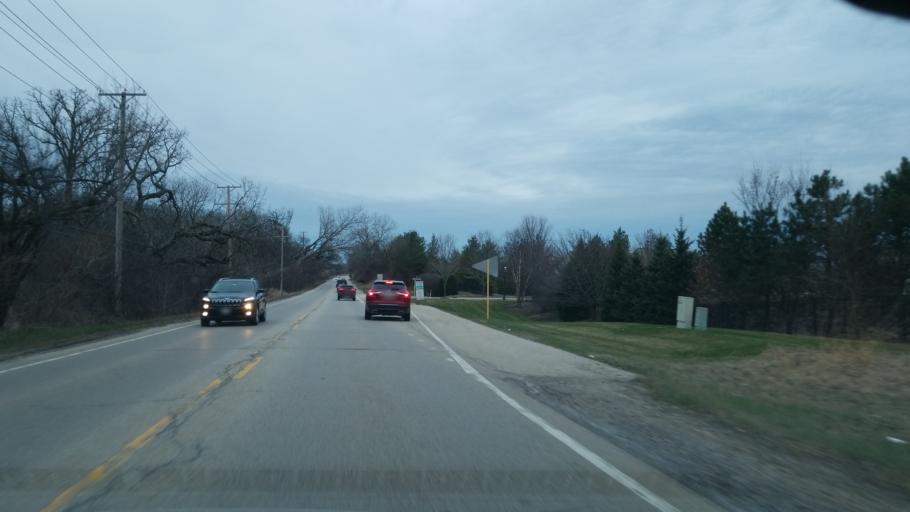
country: US
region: Illinois
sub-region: Kane County
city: Sleepy Hollow
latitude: 42.1032
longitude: -88.3243
